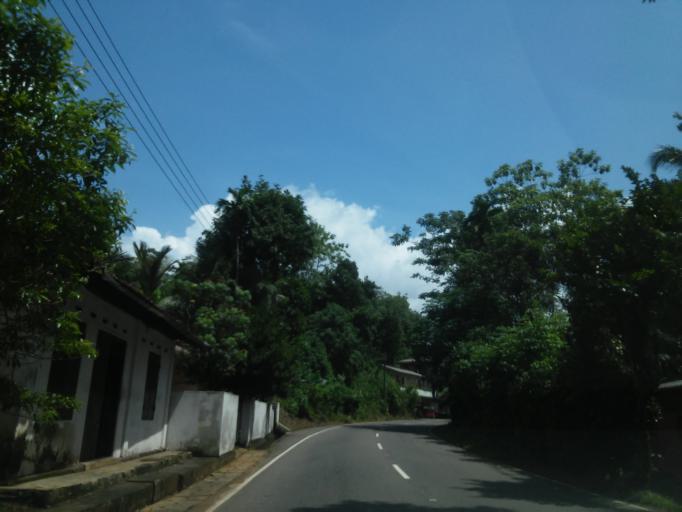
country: LK
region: Sabaragamuwa
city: Ratnapura
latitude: 6.7291
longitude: 80.3191
